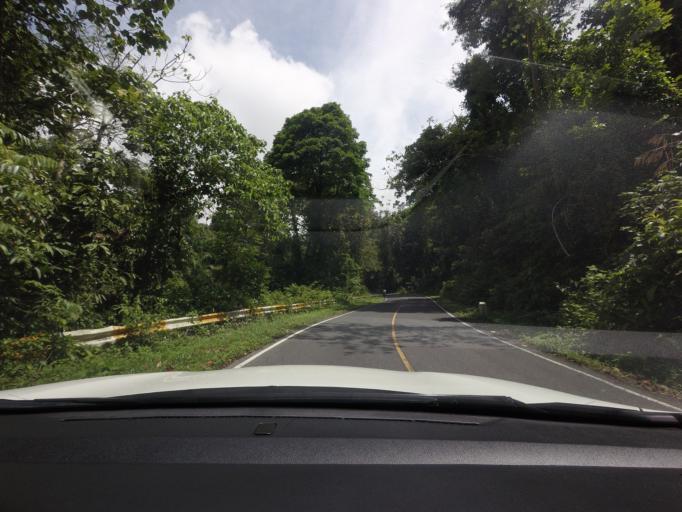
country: TH
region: Nakhon Nayok
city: Pak Phli
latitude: 14.3202
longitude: 101.3719
